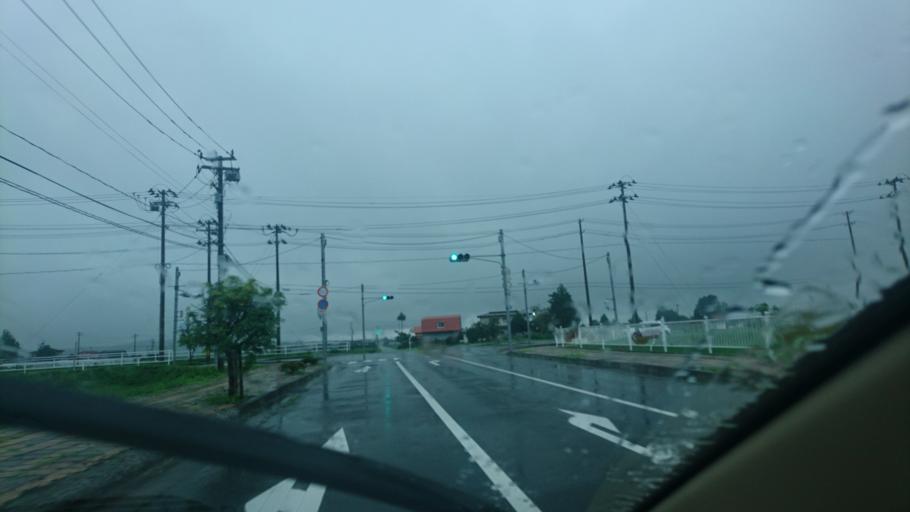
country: JP
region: Iwate
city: Mizusawa
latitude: 39.1784
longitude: 141.1812
